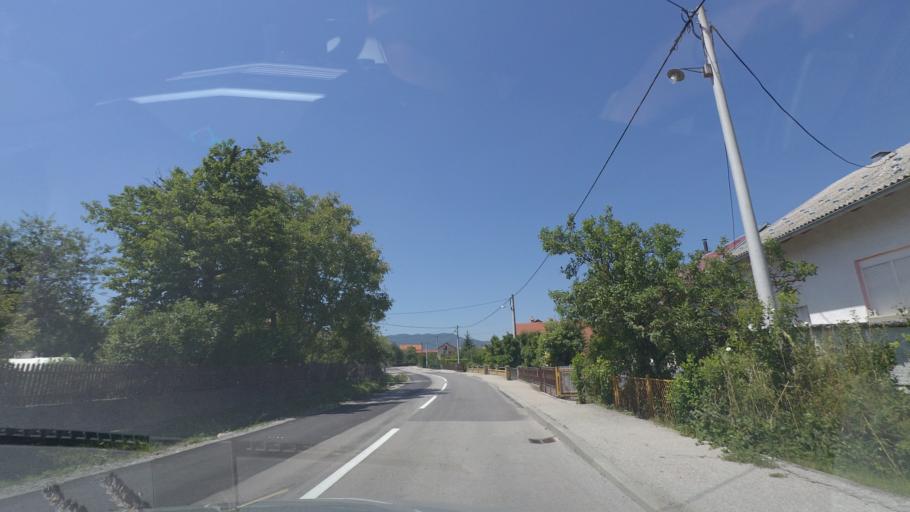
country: HR
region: Grad Zagreb
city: Horvati
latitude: 45.6797
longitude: 15.7537
